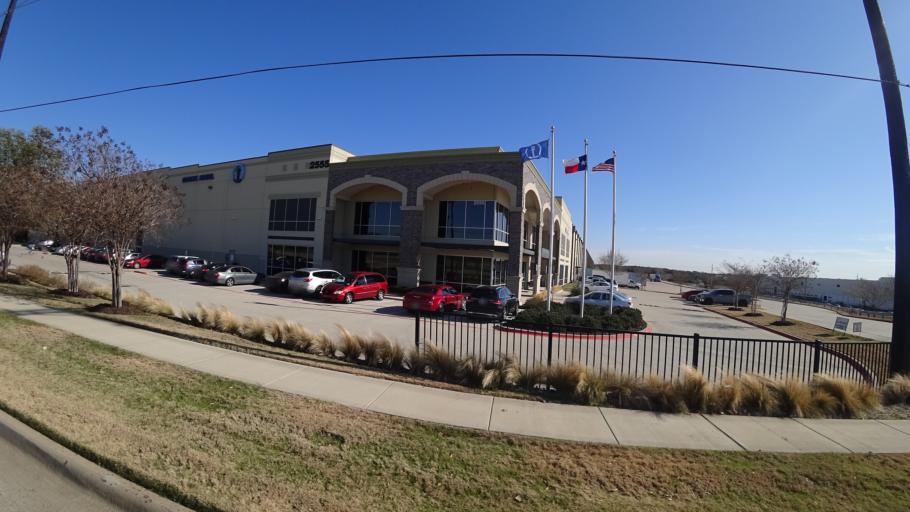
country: US
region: Texas
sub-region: Dallas County
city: Coppell
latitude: 33.0004
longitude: -97.0157
